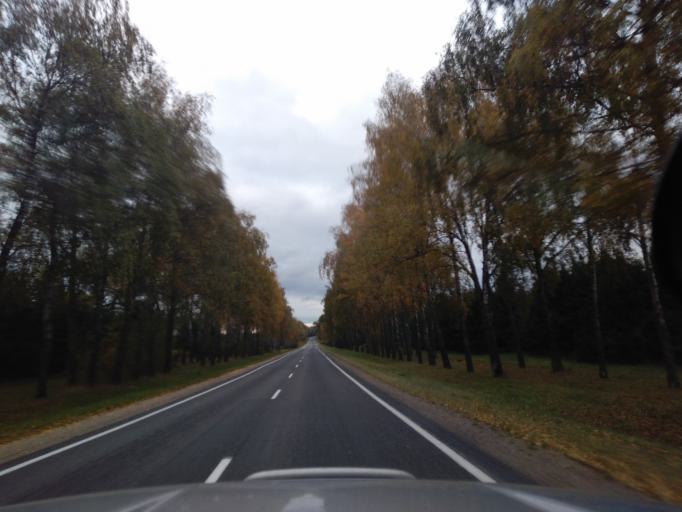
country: BY
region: Minsk
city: Slutsk
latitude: 53.2209
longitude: 27.4801
